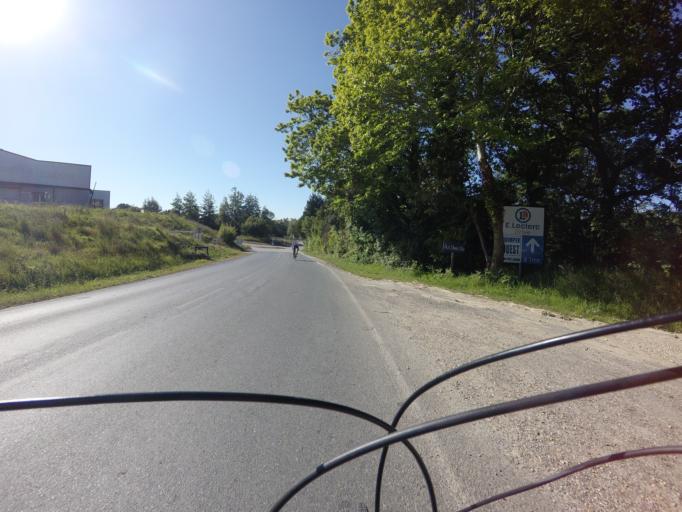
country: FR
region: Brittany
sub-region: Departement du Finistere
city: Plomelin
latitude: 47.9673
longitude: -4.1445
